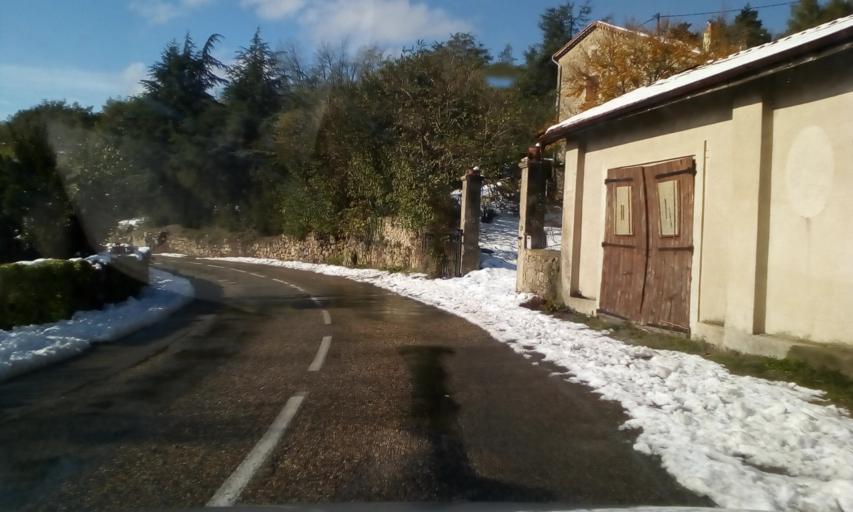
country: FR
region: Rhone-Alpes
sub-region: Departement de l'Ardeche
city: Saint-Felicien
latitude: 45.1001
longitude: 4.6682
